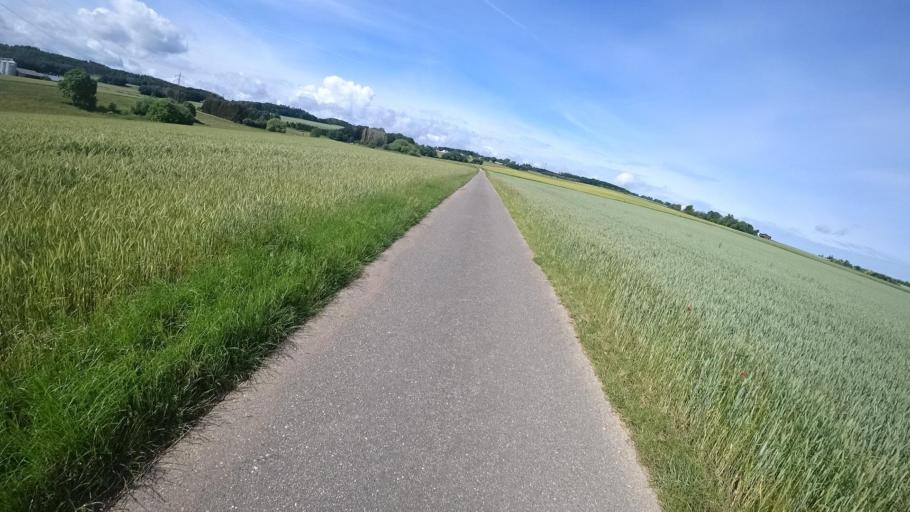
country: DE
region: Rheinland-Pfalz
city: Mayschoss
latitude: 50.5525
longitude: 7.0204
